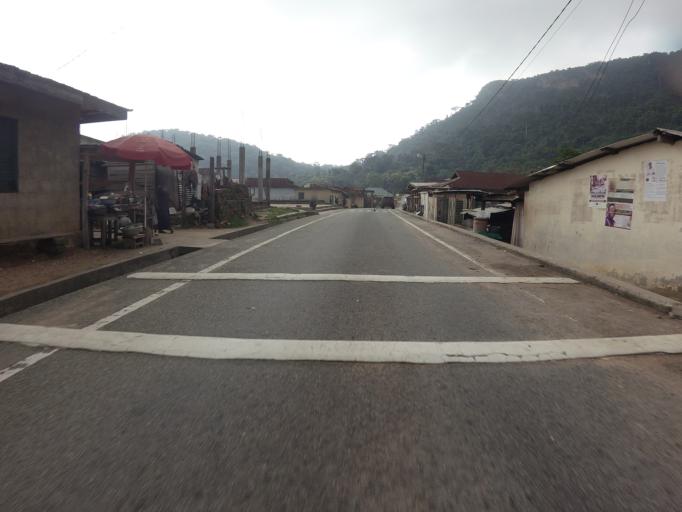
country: GH
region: Volta
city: Kpandu
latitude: 6.8222
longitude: 0.4252
